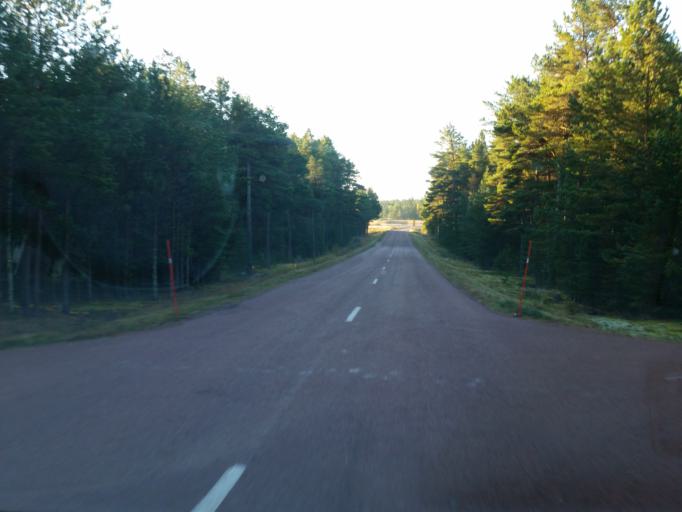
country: AX
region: Alands skaergard
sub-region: Vardoe
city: Vardoe
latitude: 60.2749
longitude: 20.3899
